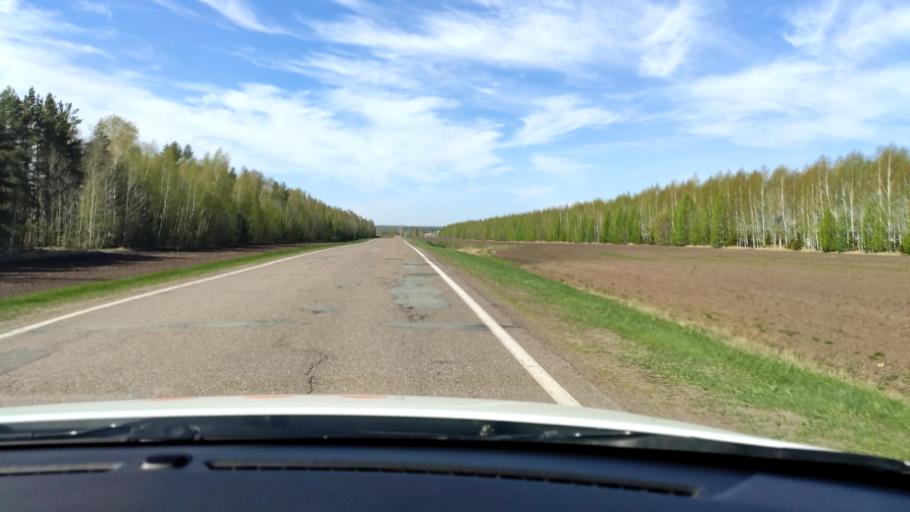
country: RU
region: Tatarstan
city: Stolbishchi
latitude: 55.5383
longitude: 49.2191
